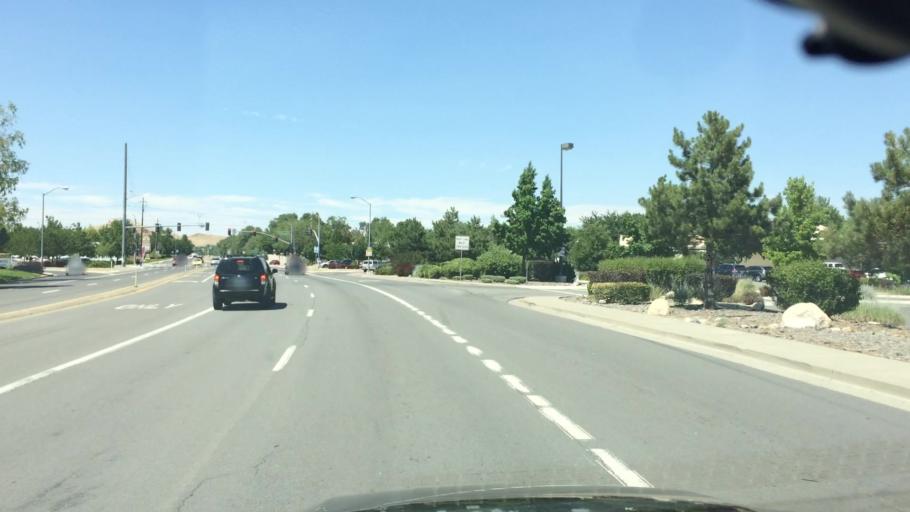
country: US
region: Nevada
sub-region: Washoe County
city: Sparks
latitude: 39.5404
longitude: -119.7337
